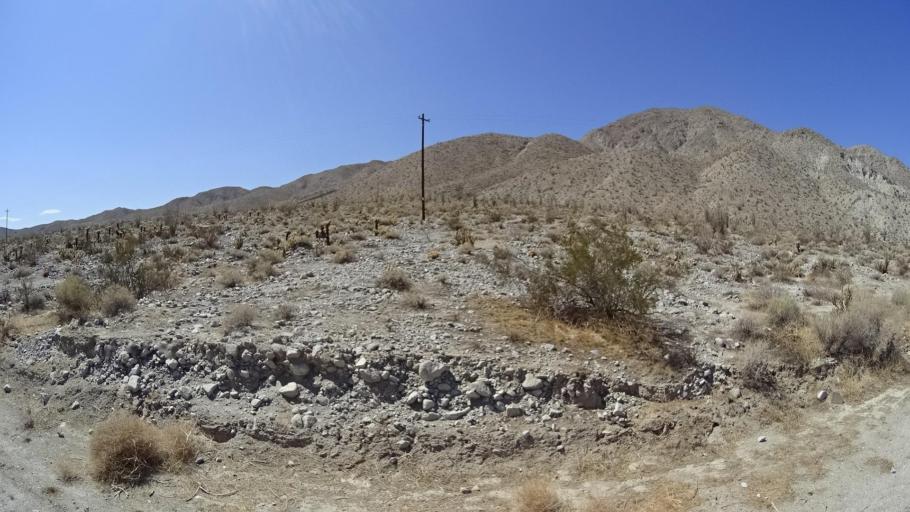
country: US
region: California
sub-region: San Diego County
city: Pine Valley
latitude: 32.9391
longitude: -116.2705
